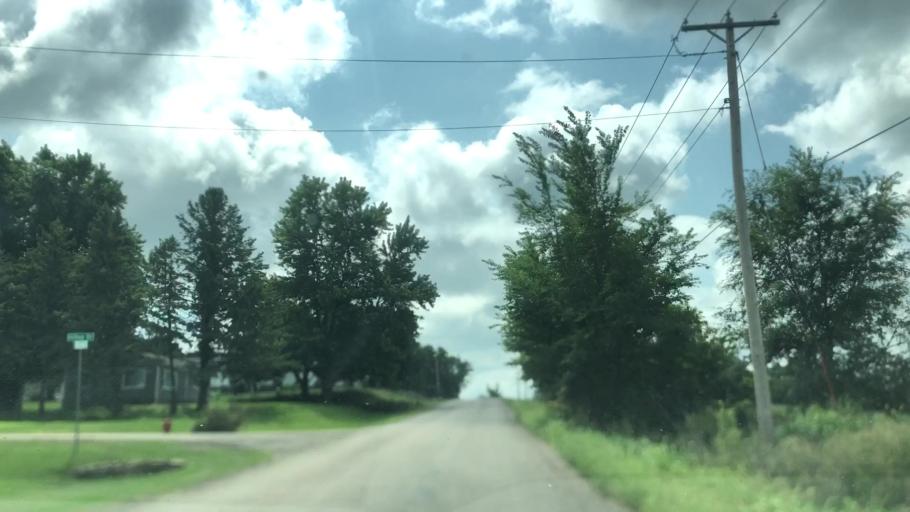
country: US
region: Iowa
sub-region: Marshall County
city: Marshalltown
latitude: 42.0510
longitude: -92.9565
